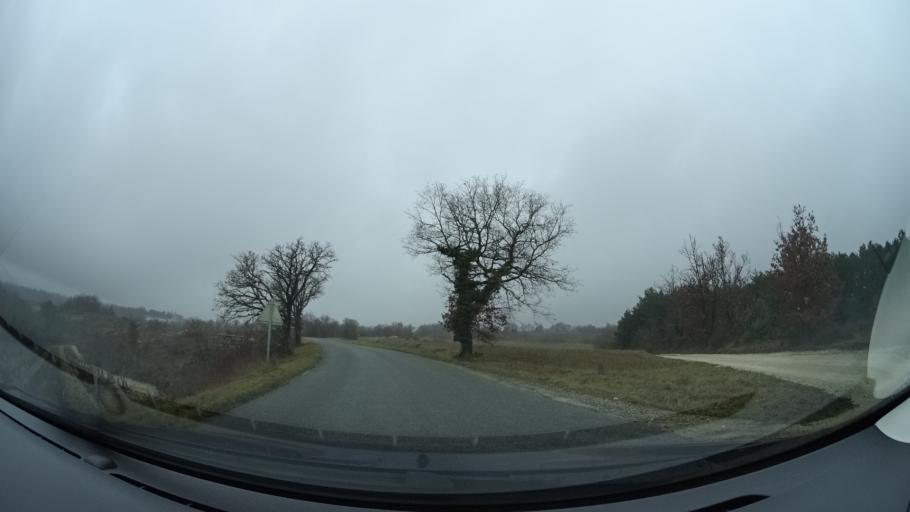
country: FR
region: Midi-Pyrenees
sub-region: Departement du Lot
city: Montcuq
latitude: 44.3770
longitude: 1.2248
